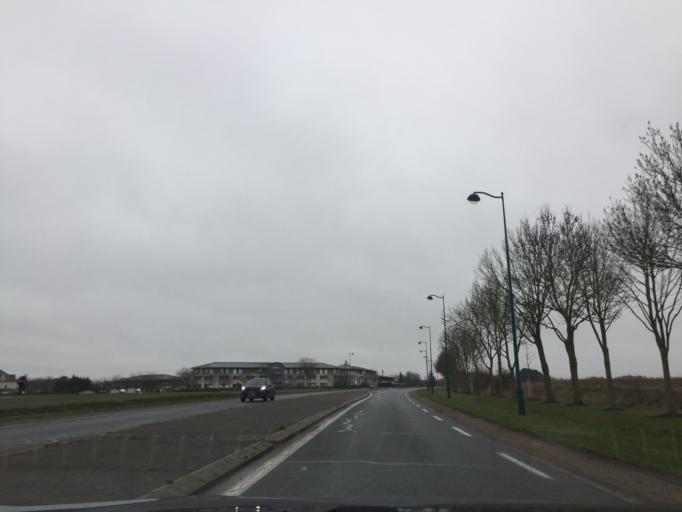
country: FR
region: Ile-de-France
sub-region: Departement de Seine-et-Marne
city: Magny-le-Hongre
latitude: 48.8688
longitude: 2.8070
